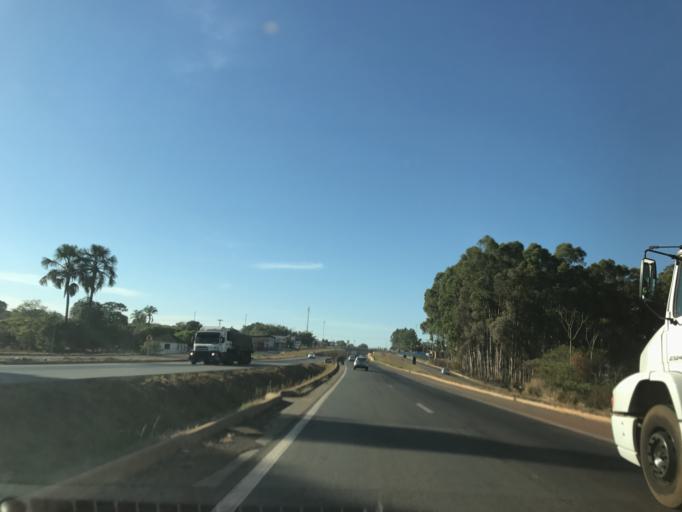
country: BR
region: Goias
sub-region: Hidrolandia
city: Hidrolandia
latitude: -16.9621
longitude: -49.2371
